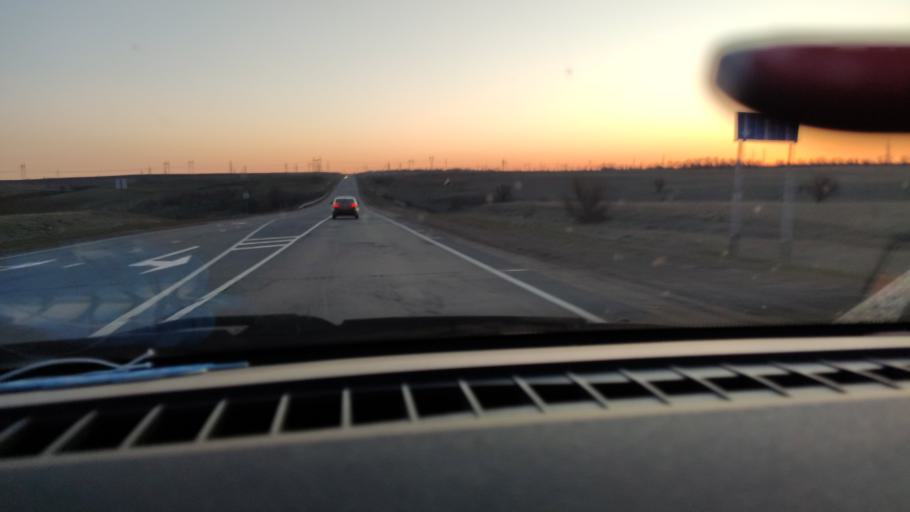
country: RU
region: Saratov
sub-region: Saratovskiy Rayon
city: Saratov
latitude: 51.7544
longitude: 46.0640
